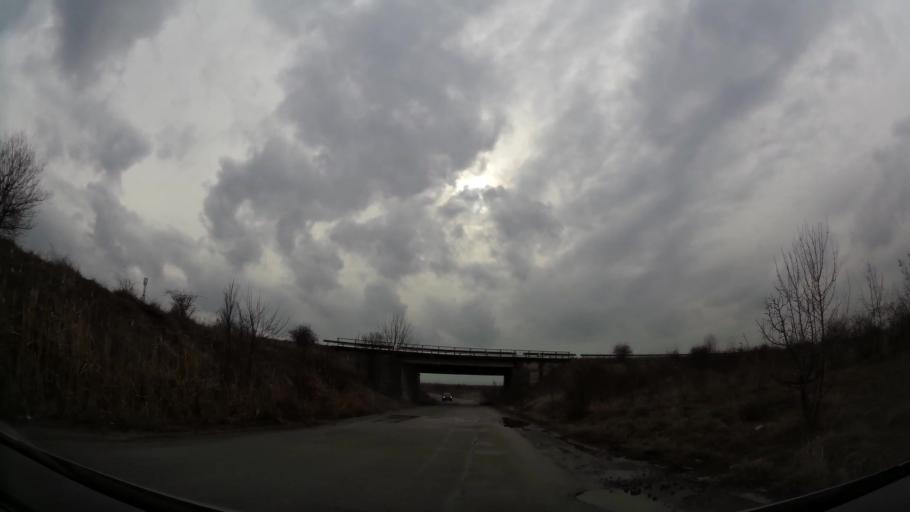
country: BG
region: Sofiya
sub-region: Obshtina Bozhurishte
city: Bozhurishte
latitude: 42.7148
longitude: 23.2206
